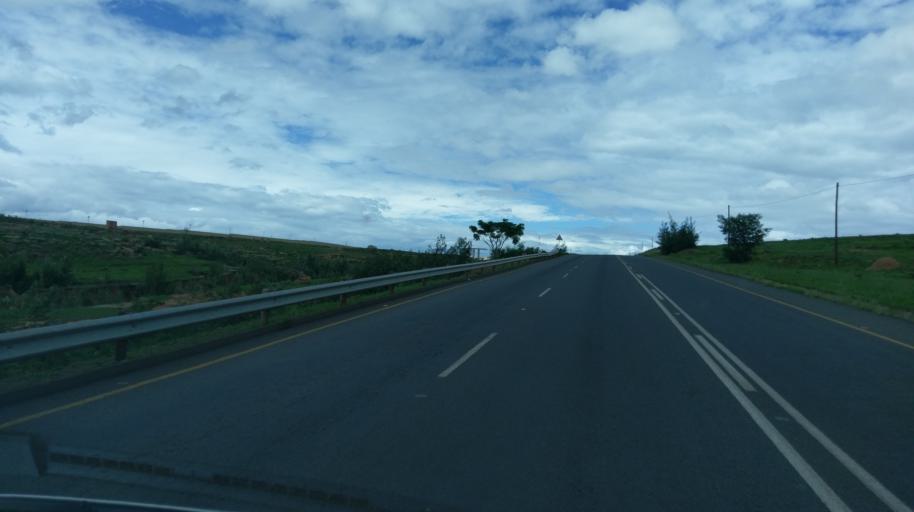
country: LS
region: Maseru
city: Maseru
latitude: -29.3948
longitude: 27.5089
